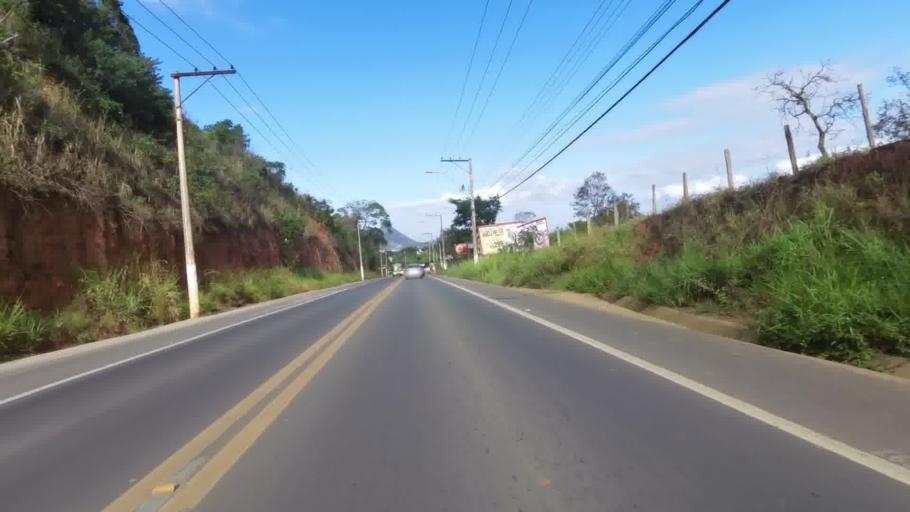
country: BR
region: Espirito Santo
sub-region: Piuma
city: Piuma
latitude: -20.8354
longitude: -40.7159
